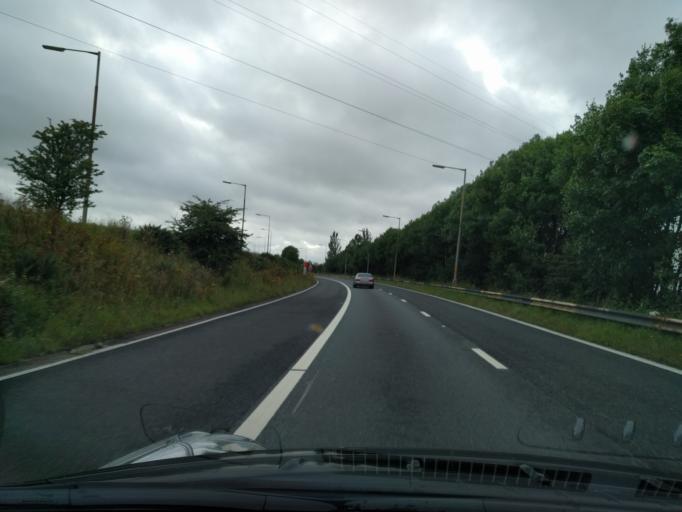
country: GB
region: England
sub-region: Warrington
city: Croft
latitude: 53.4295
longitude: -2.5555
